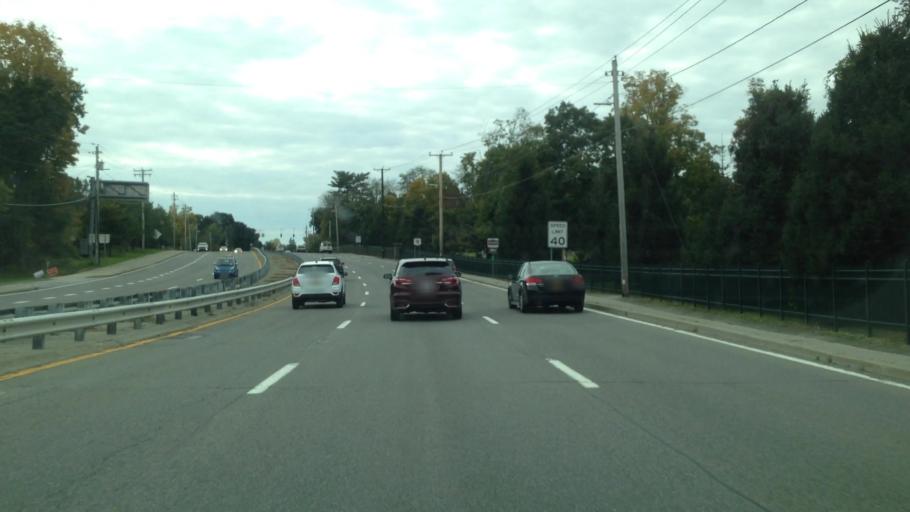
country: US
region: New York
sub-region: Dutchess County
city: Poughkeepsie
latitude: 41.6801
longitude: -73.9295
